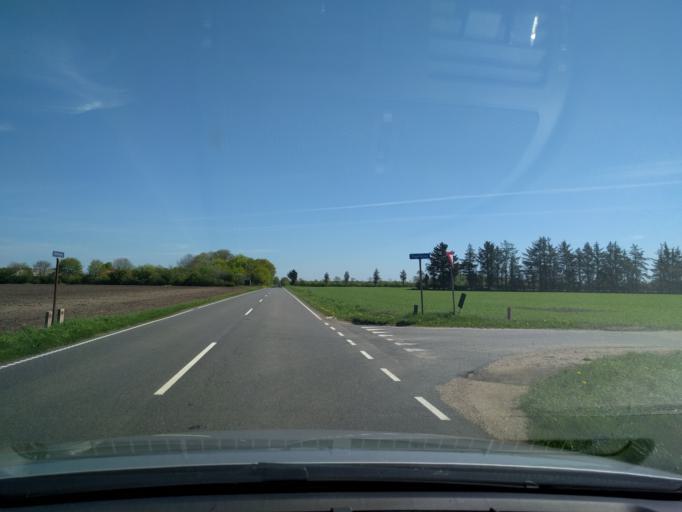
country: DK
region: South Denmark
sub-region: Billund Kommune
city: Grindsted
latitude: 55.6786
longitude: 8.9210
